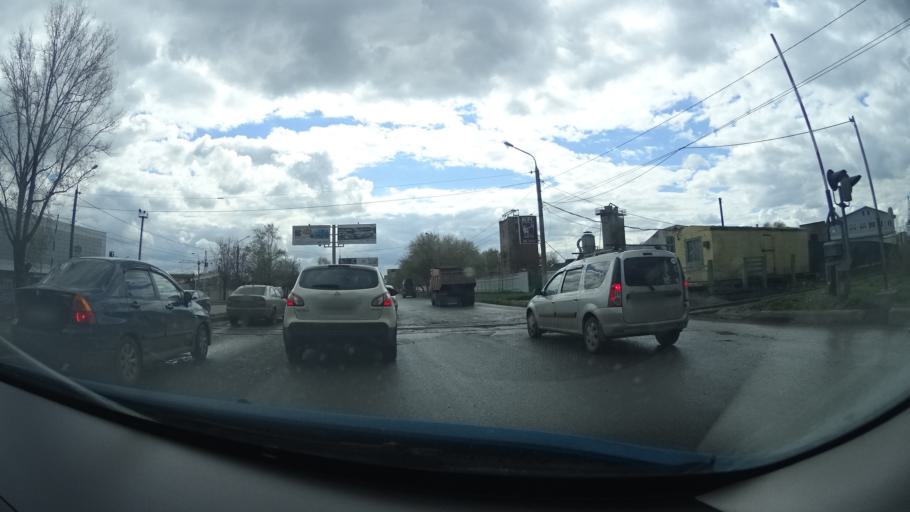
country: RU
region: Bashkortostan
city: Ufa
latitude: 54.8037
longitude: 56.0815
